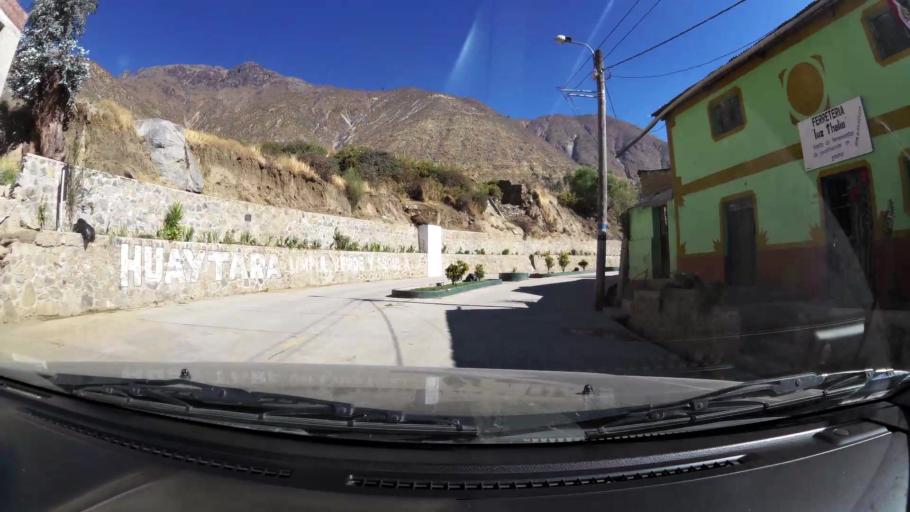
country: PE
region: Huancavelica
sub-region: Huaytara
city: Quito-Arma
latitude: -13.6036
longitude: -75.3489
